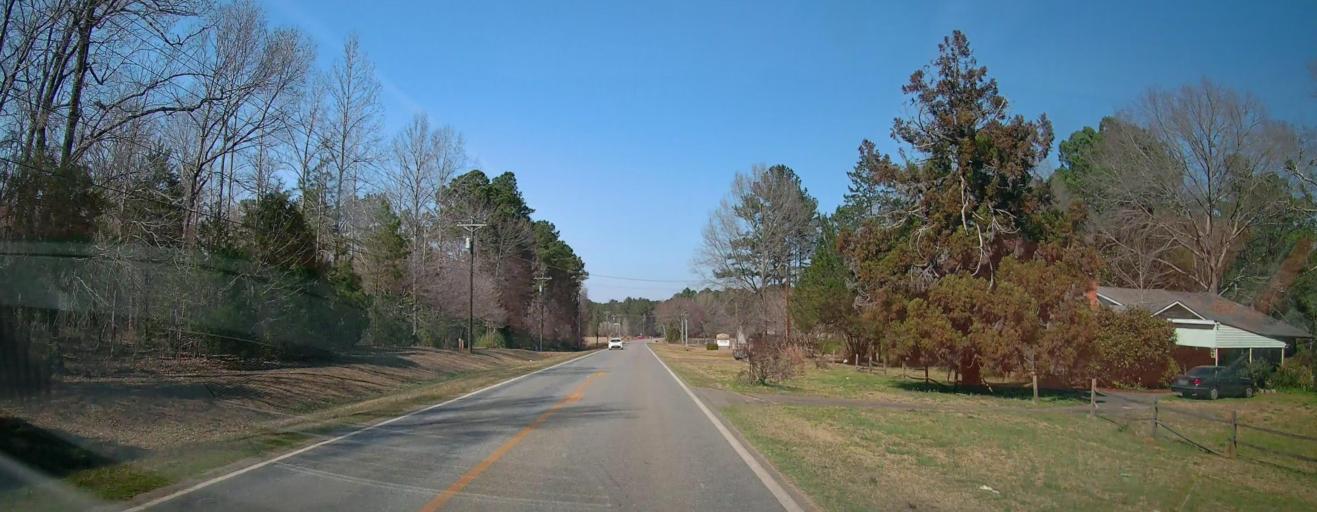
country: US
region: Georgia
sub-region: Jones County
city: Gray
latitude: 32.9658
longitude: -83.5471
